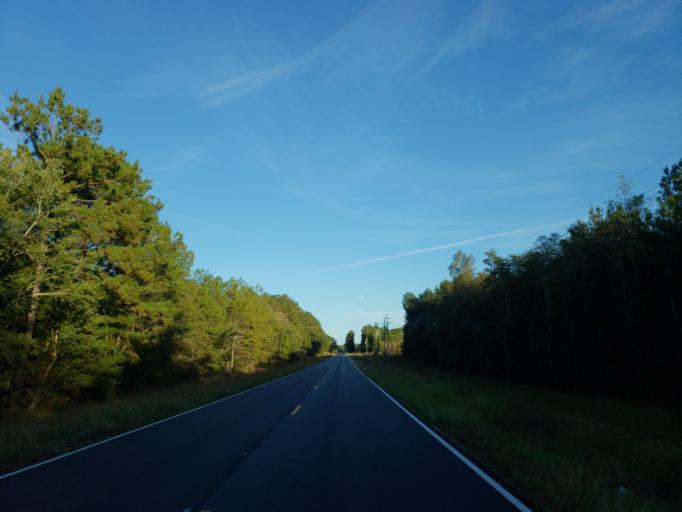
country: US
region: Mississippi
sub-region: Wayne County
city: Belmont
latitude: 31.4212
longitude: -88.5285
